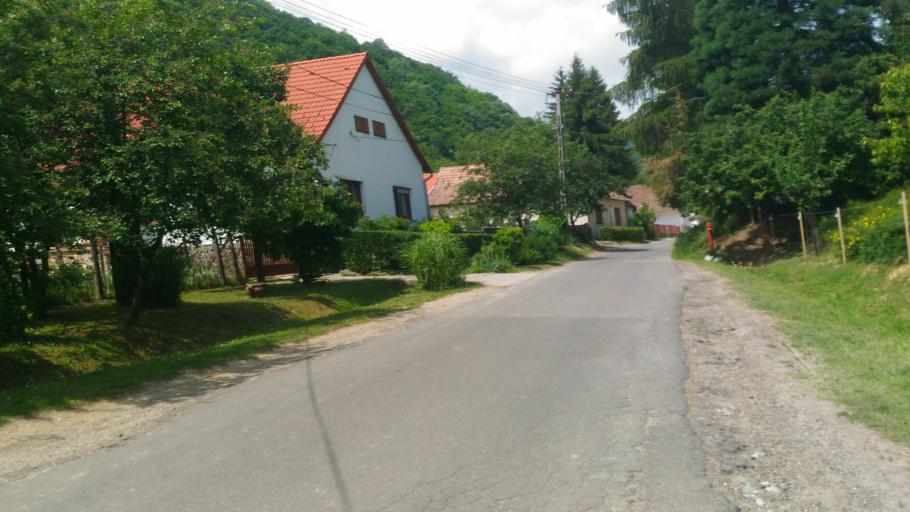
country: HU
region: Baranya
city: Mecseknadasd
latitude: 46.2201
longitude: 18.4129
